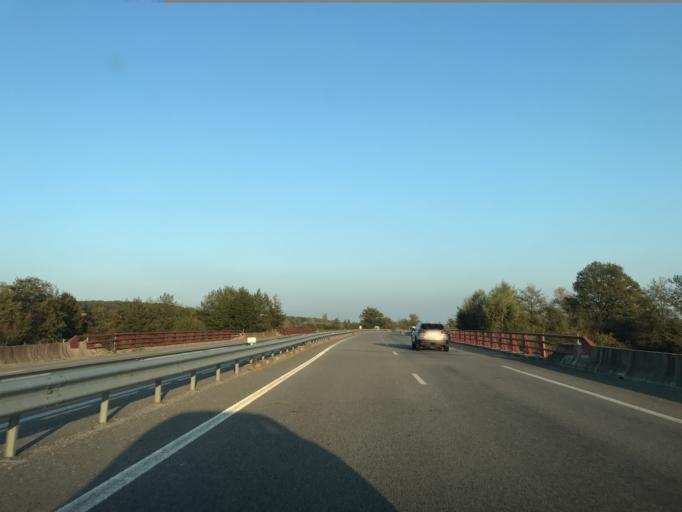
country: FR
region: Lower Normandy
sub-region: Departement de l'Orne
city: Valframbert
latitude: 48.4796
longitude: 0.2232
